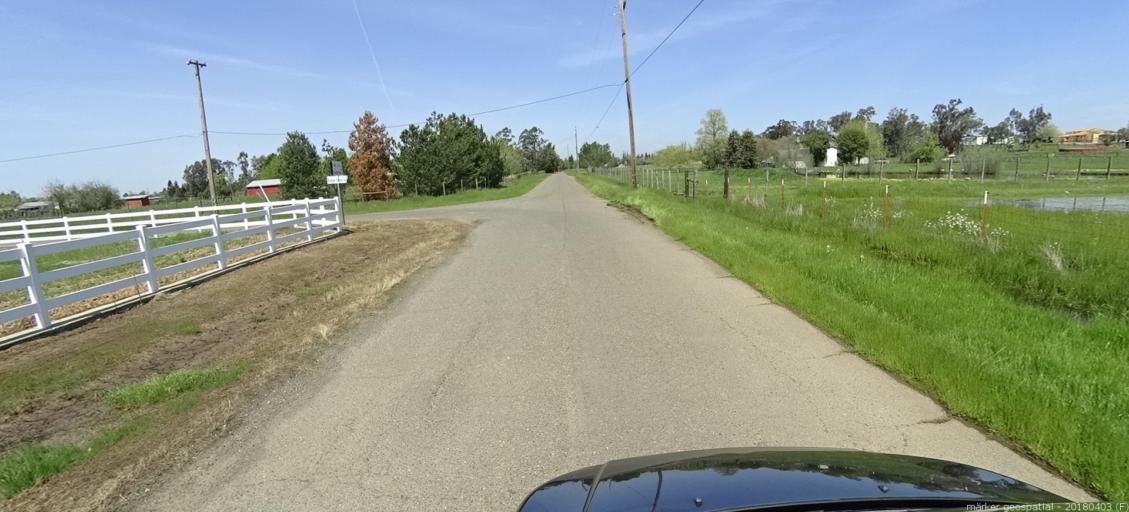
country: US
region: California
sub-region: Sacramento County
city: Wilton
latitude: 38.3902
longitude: -121.2468
